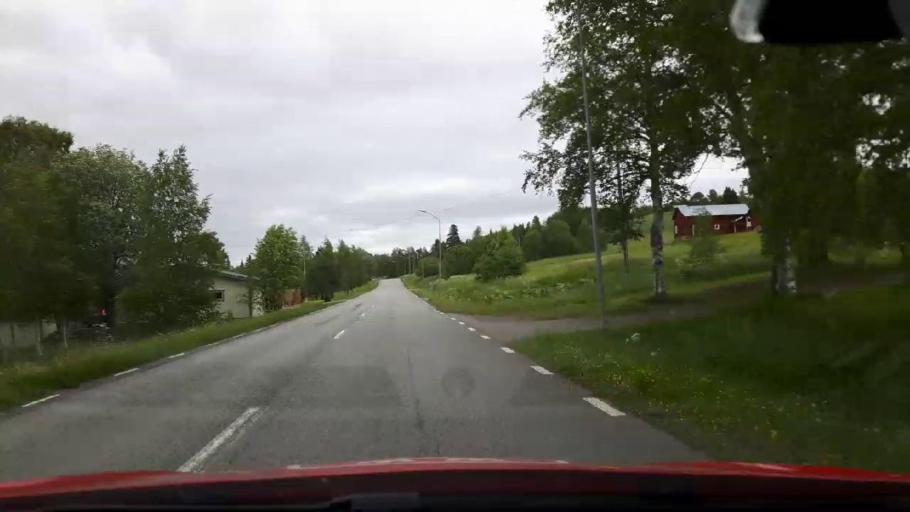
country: SE
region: Jaemtland
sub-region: Stroemsunds Kommun
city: Stroemsund
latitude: 63.5752
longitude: 15.3757
